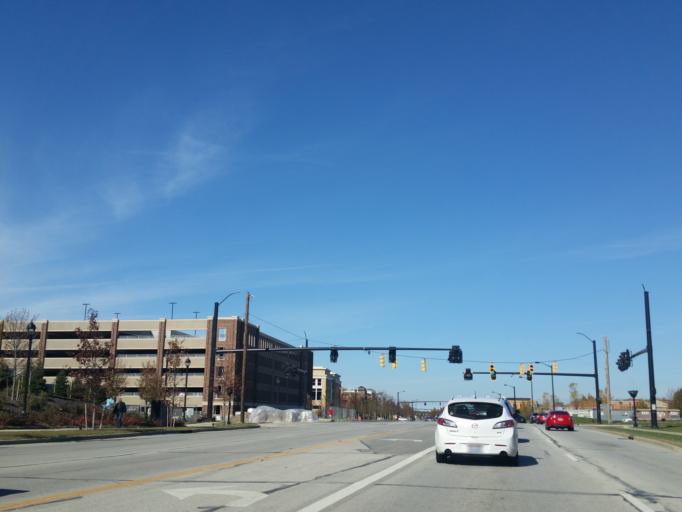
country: US
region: Ohio
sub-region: Cuyahoga County
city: Westlake
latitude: 41.4549
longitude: -81.9493
